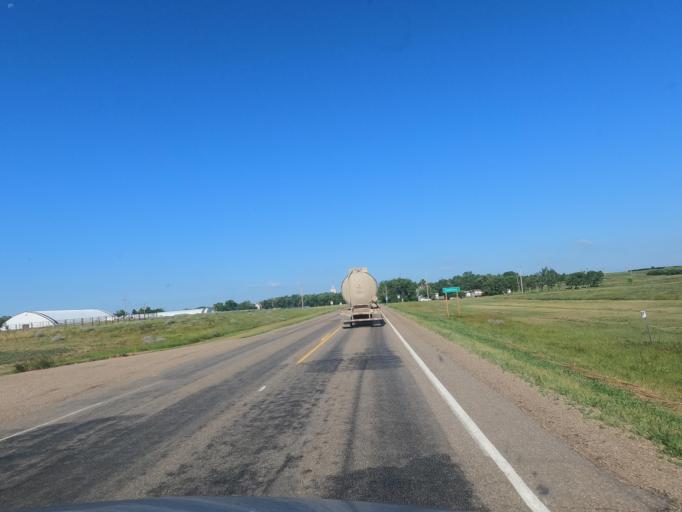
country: CA
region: Saskatchewan
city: Swift Current
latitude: 49.7278
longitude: -107.7341
